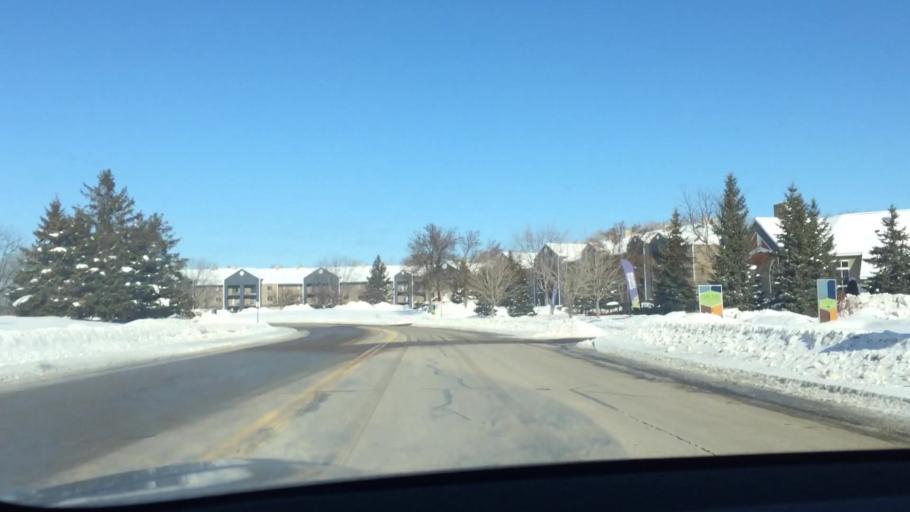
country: US
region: Minnesota
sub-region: Hennepin County
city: Plymouth
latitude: 45.0194
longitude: -93.4644
